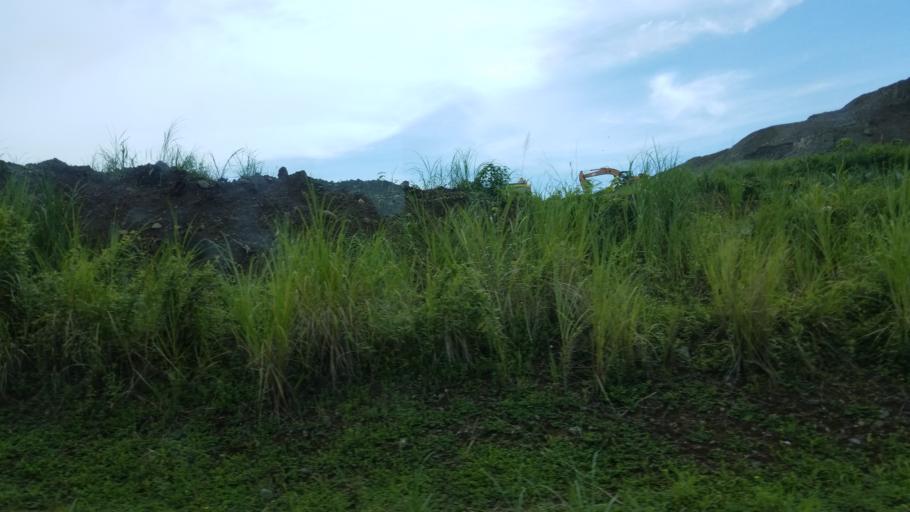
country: PA
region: Panama
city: San Miguelito
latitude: 9.1004
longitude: -79.4748
